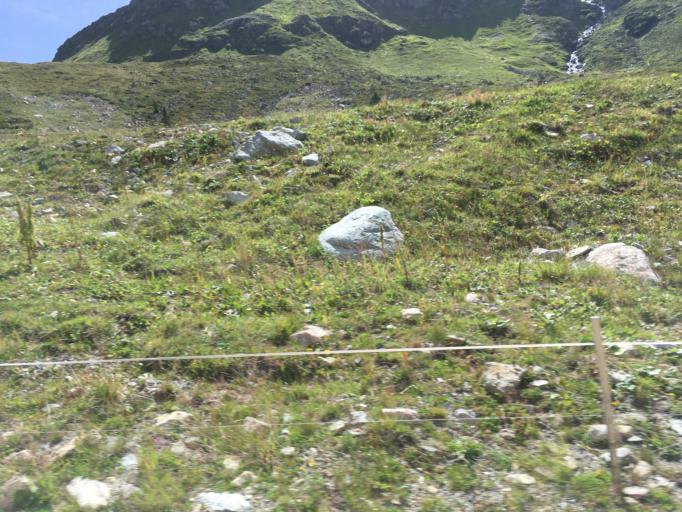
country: CH
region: Grisons
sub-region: Maloja District
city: Silvaplana
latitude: 46.4651
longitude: 9.7061
